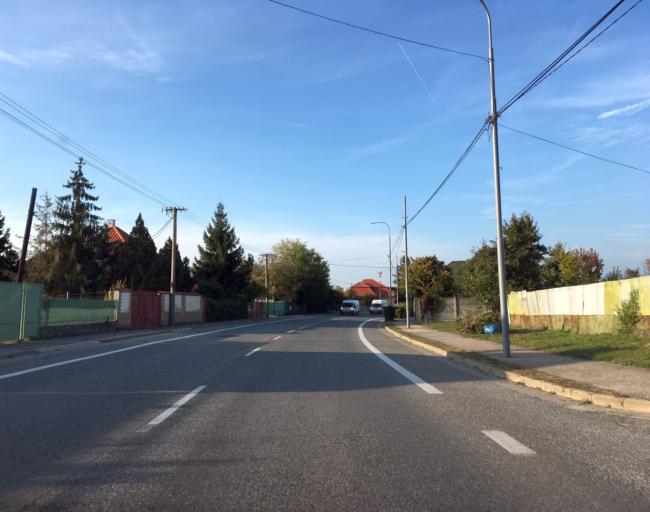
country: SK
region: Nitriansky
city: Surany
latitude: 48.0970
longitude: 18.0621
